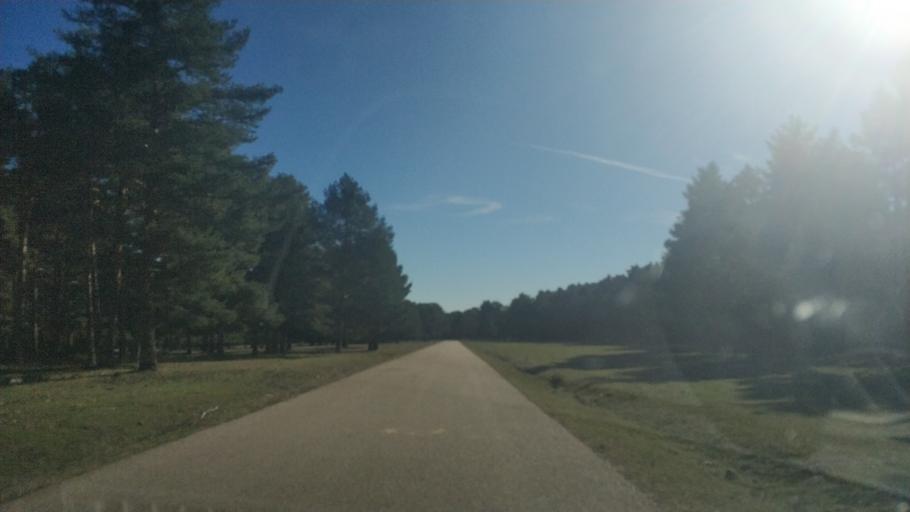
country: ES
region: Castille and Leon
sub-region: Provincia de Soria
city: Vinuesa
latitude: 41.9575
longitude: -2.7837
